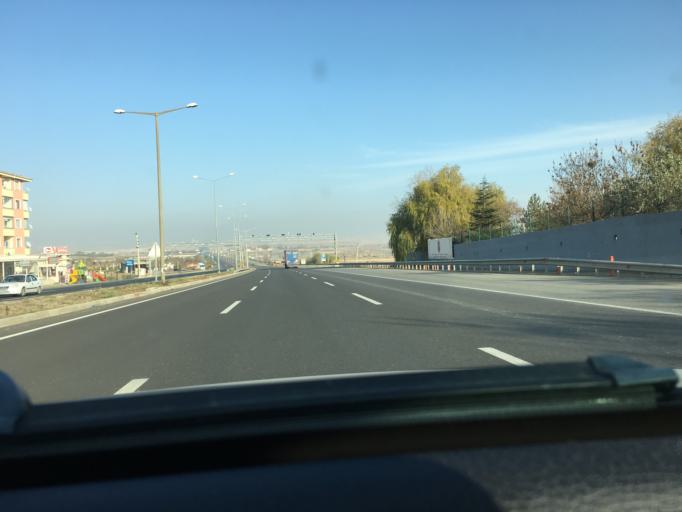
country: TR
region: Ankara
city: Temelli
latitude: 39.7245
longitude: 32.3546
